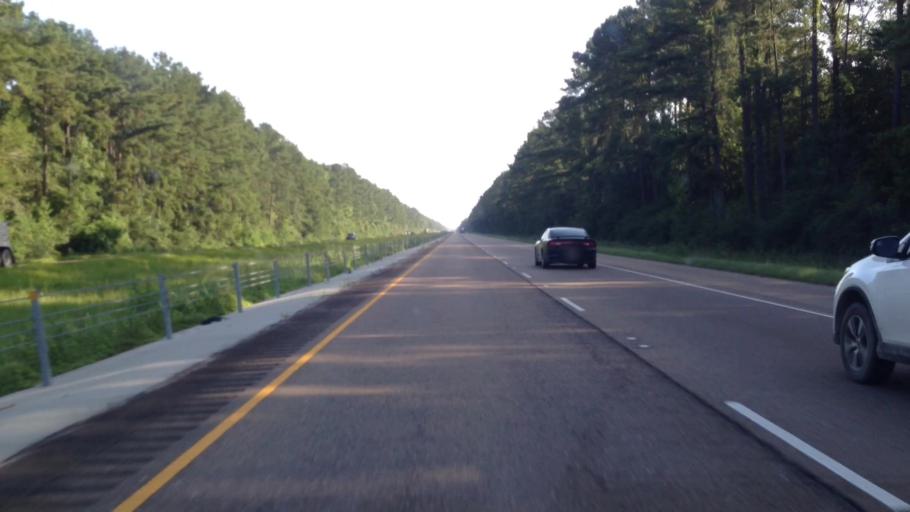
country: US
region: Louisiana
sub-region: Tangipahoa Parish
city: Independence
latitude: 30.6779
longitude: -90.5326
